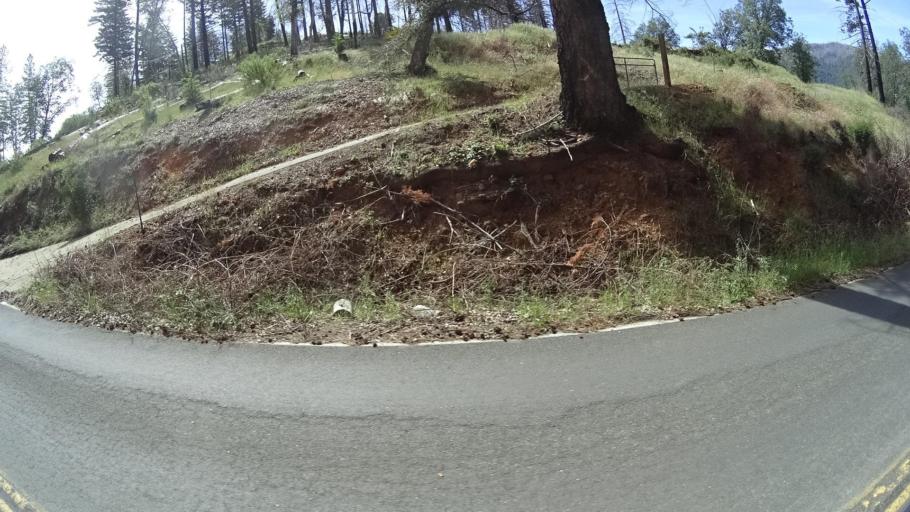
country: US
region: California
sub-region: Lake County
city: Cobb
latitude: 38.8467
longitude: -122.7295
